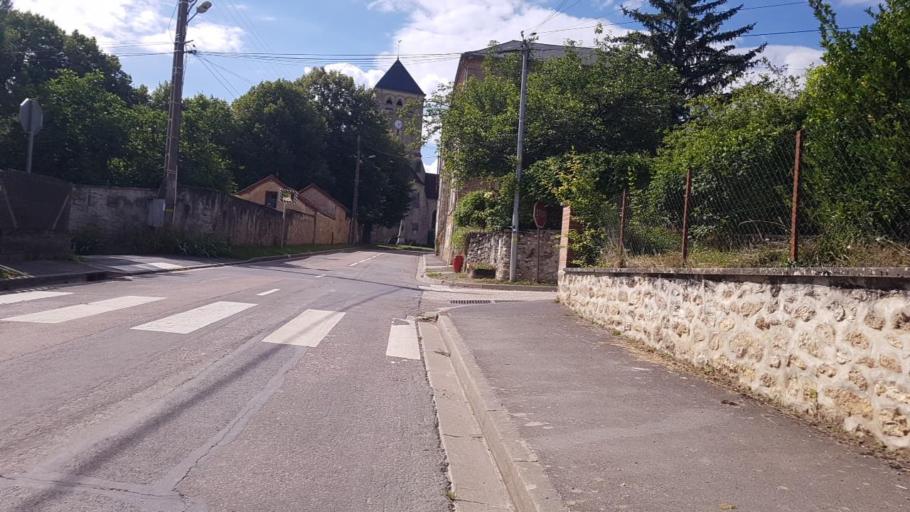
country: FR
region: Picardie
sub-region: Departement de l'Aisne
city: Crezancy
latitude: 49.0856
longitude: 3.5535
